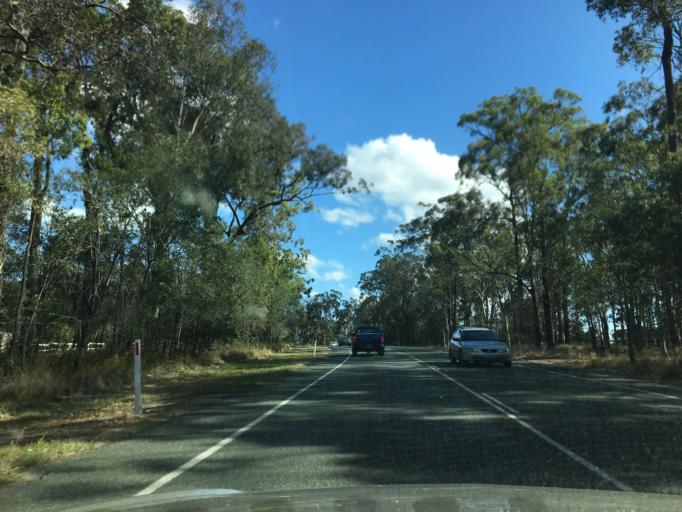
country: AU
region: Queensland
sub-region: Logan
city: Chambers Flat
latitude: -27.7923
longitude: 153.0995
